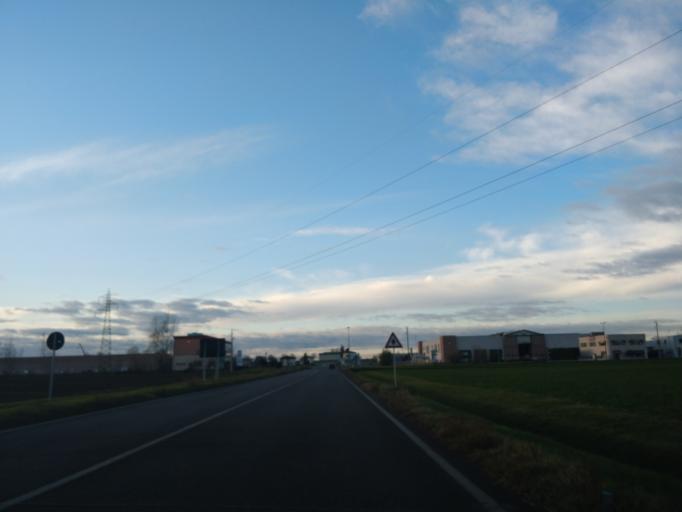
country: IT
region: Emilia-Romagna
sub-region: Provincia di Ferrara
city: Cento
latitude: 44.7447
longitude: 11.2812
